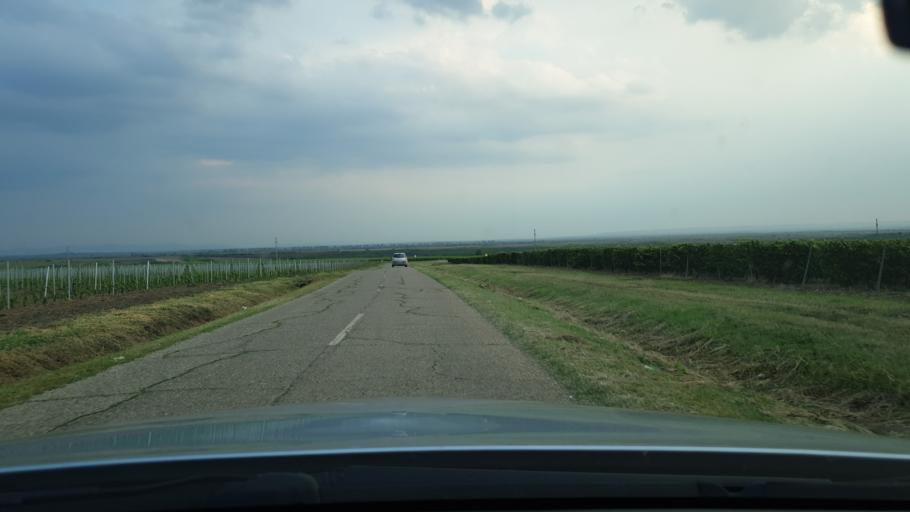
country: RS
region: Autonomna Pokrajina Vojvodina
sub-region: Juznobanatski Okrug
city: Vrsac
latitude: 45.1026
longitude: 21.3280
